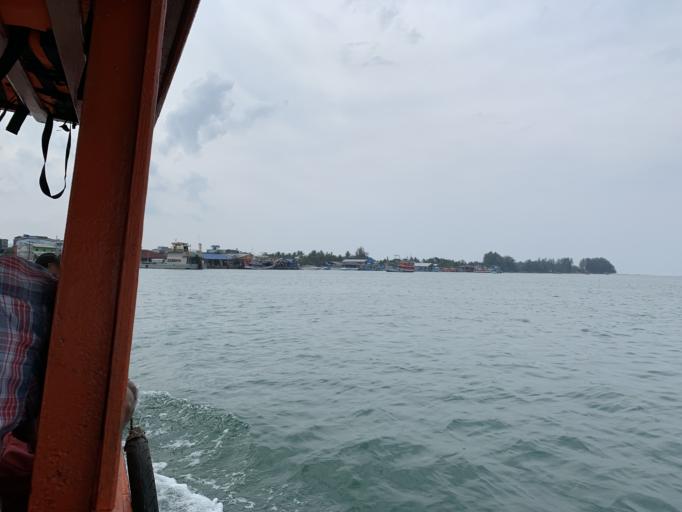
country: TH
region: Phangnga
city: Takua Pa
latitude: 8.8672
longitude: 98.2737
